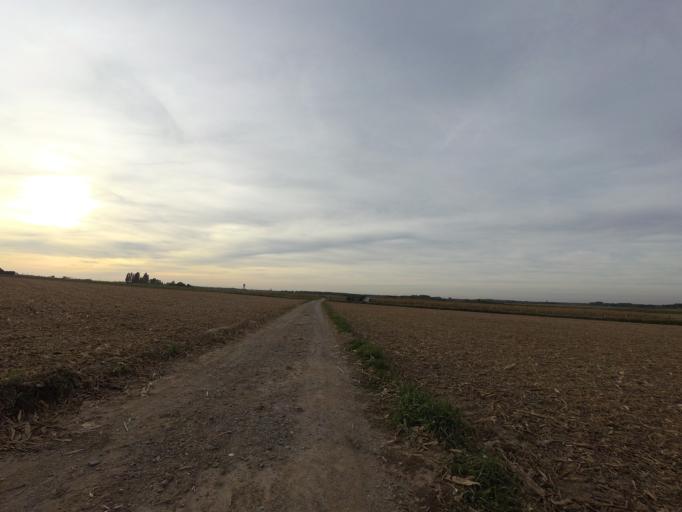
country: BE
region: Flanders
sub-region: Provincie Vlaams-Brabant
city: Kortenberg
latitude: 50.9058
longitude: 4.5516
